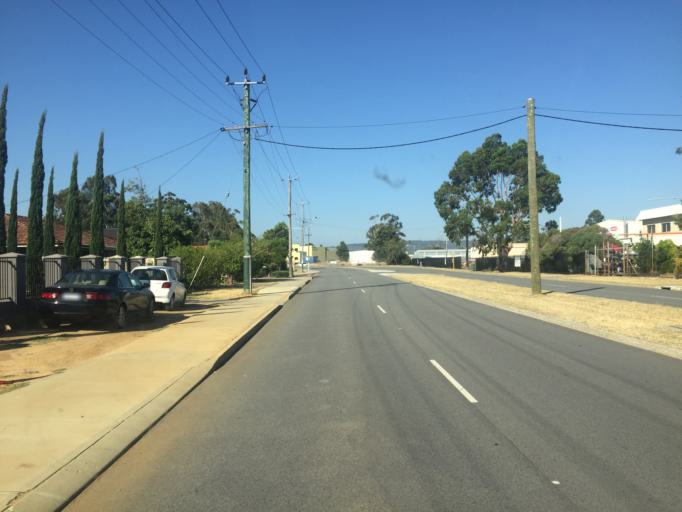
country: AU
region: Western Australia
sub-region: Gosnells
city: Maddington
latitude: -32.0423
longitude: 115.9805
